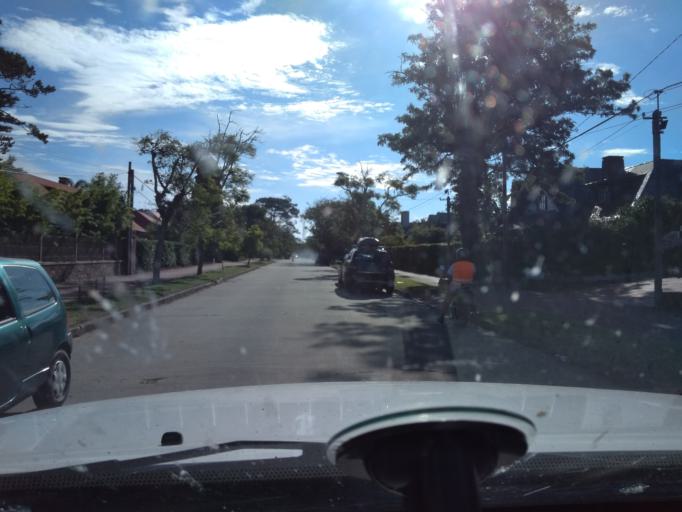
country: UY
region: Canelones
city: Paso de Carrasco
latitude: -34.8886
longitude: -56.0605
